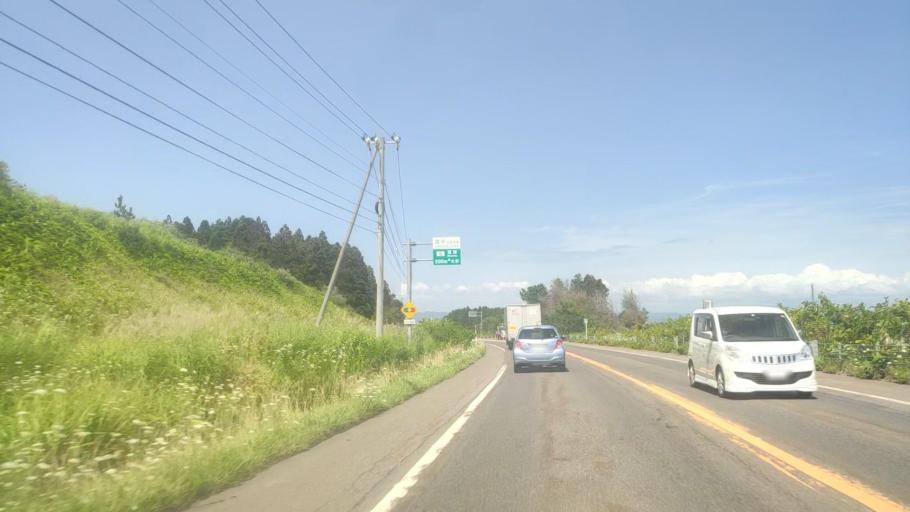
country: JP
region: Hokkaido
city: Nanae
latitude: 42.2072
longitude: 140.4033
